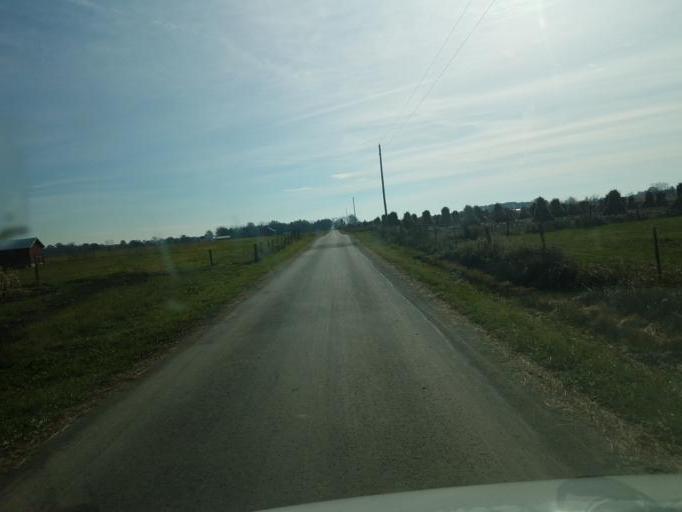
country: US
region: Ohio
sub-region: Union County
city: Richwood
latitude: 40.5625
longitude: -83.4182
